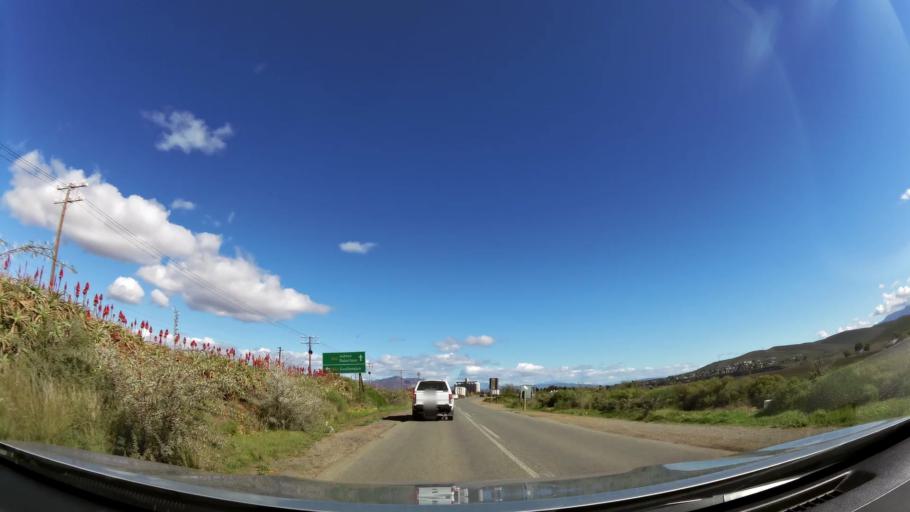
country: ZA
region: Western Cape
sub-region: Cape Winelands District Municipality
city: Ashton
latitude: -33.8299
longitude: 20.0836
